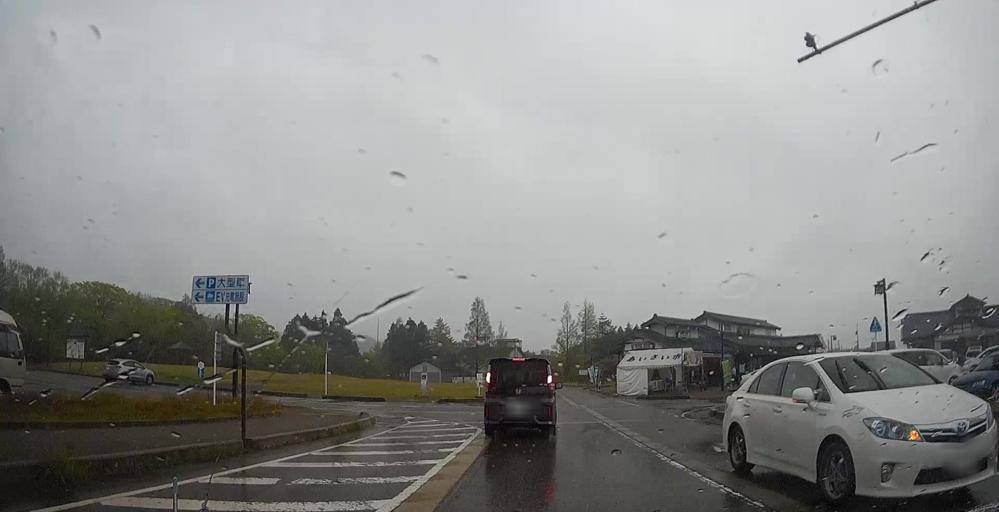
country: JP
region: Niigata
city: Murakami
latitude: 38.0920
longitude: 139.5669
